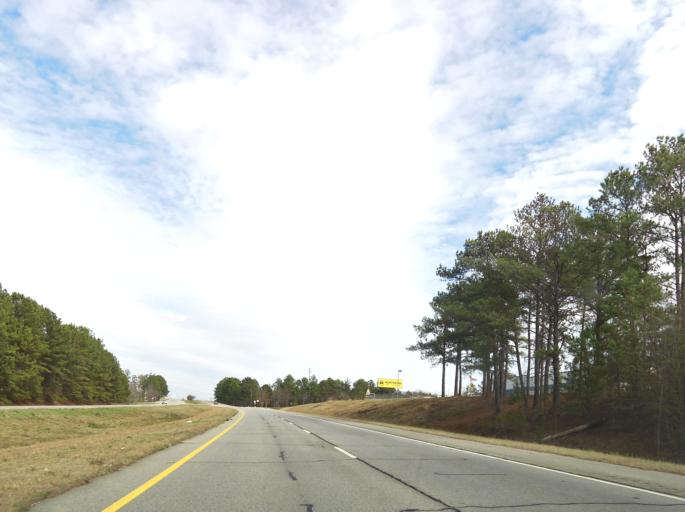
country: US
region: Georgia
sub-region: Bibb County
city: West Point
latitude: 32.8022
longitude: -83.7389
